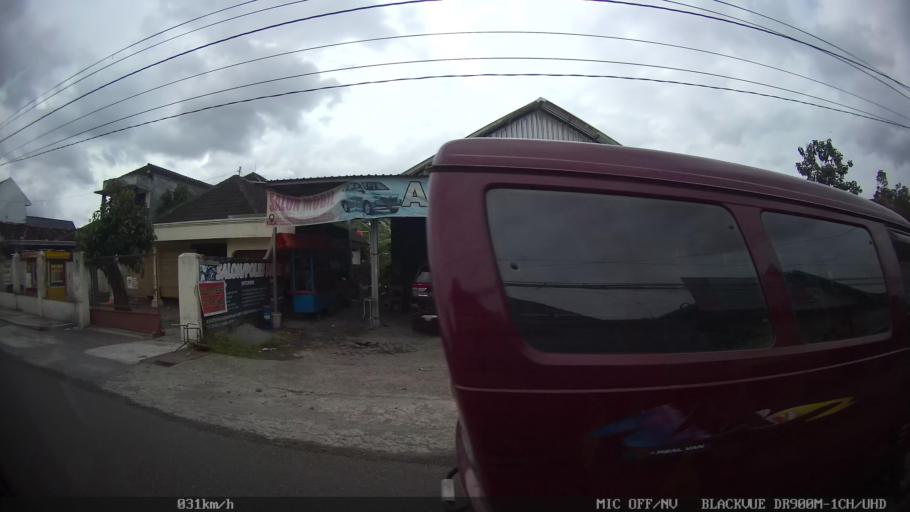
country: ID
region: Daerah Istimewa Yogyakarta
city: Depok
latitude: -7.8246
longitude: 110.4143
